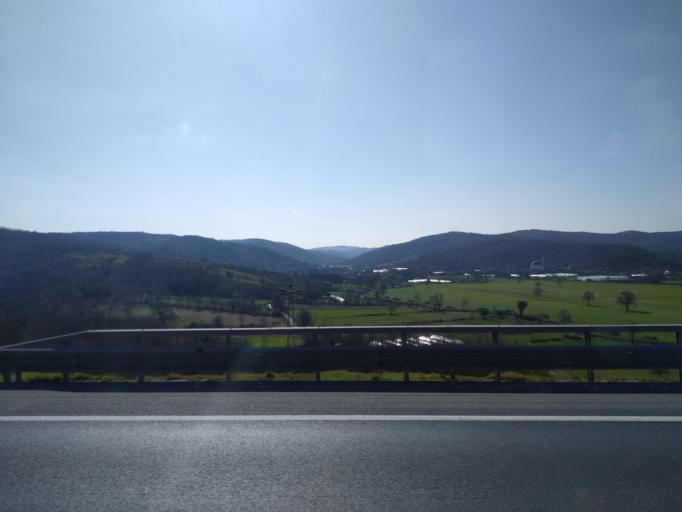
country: TR
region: Istanbul
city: Mahmut Sevket Pasa
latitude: 41.1872
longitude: 29.2141
